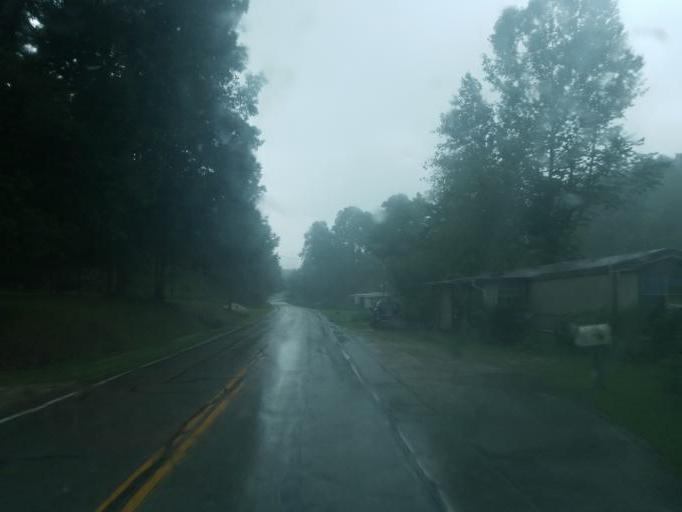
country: US
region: Kentucky
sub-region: Carter County
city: Olive Hill
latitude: 38.2792
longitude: -83.3040
